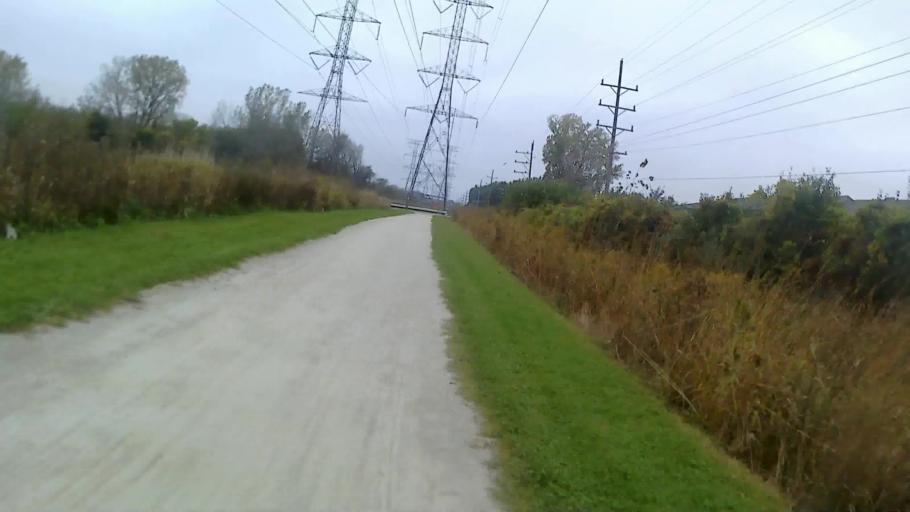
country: US
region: Illinois
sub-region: Kane County
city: Aurora
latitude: 41.7910
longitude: -88.2692
